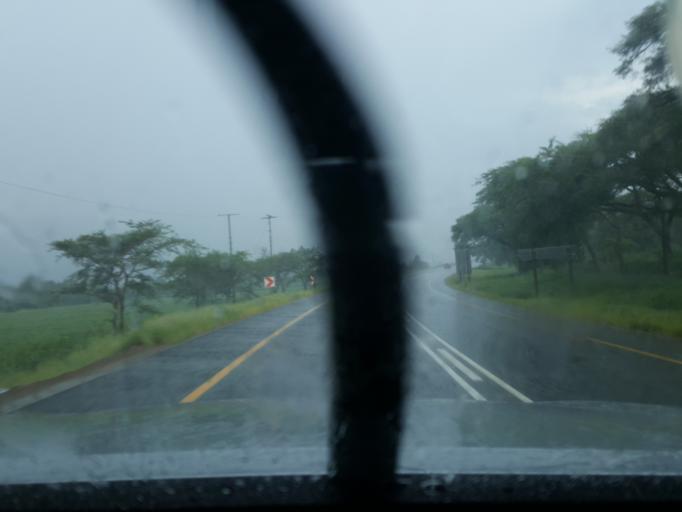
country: ZA
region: Mpumalanga
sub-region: Nkangala District Municipality
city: Belfast
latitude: -25.5966
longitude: 30.4509
